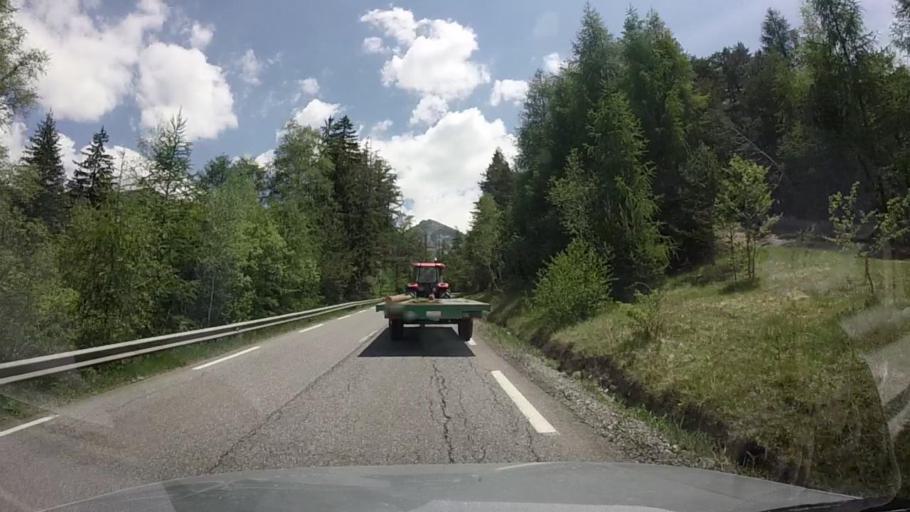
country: FR
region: Provence-Alpes-Cote d'Azur
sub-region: Departement des Alpes-de-Haute-Provence
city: Seyne-les-Alpes
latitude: 44.3247
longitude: 6.3959
